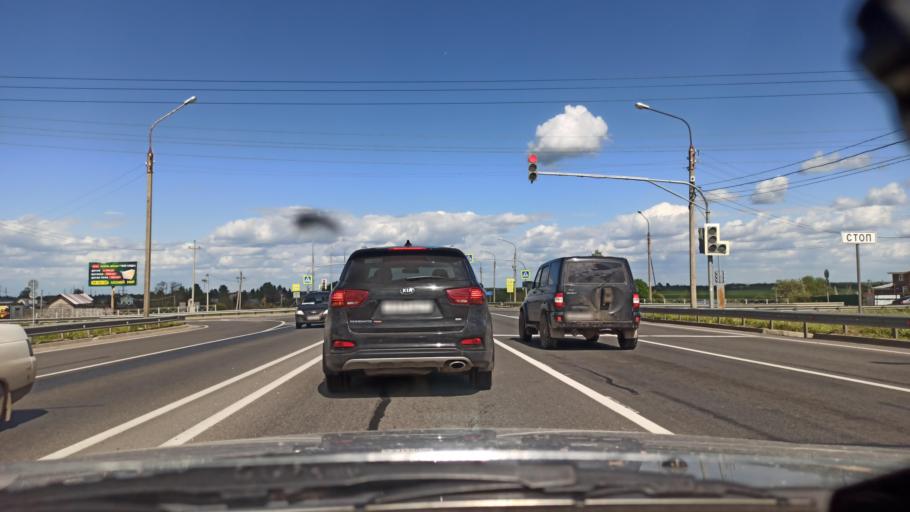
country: RU
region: Vologda
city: Vologda
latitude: 59.2875
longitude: 39.8546
